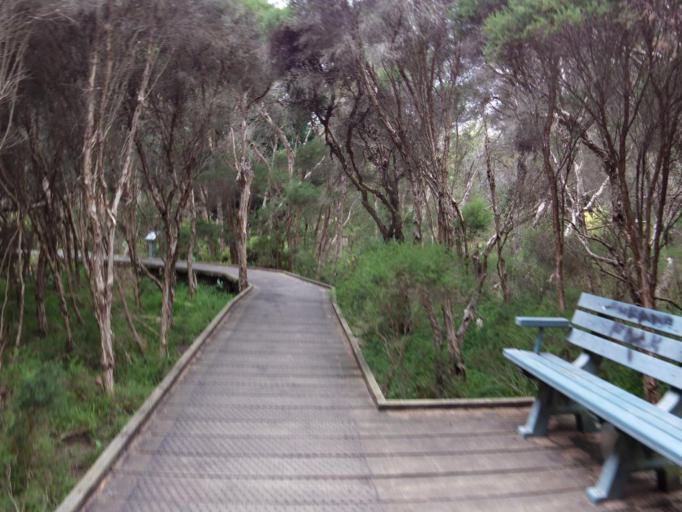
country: AU
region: Victoria
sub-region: Frankston
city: Frankston
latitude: -38.1645
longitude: 145.1113
